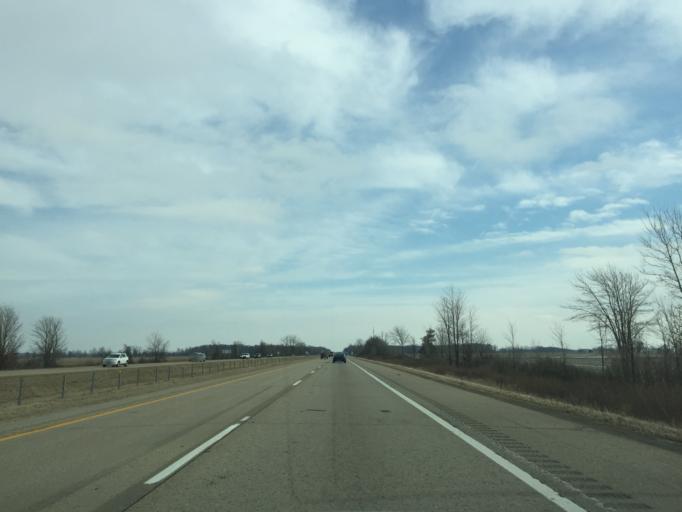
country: US
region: Michigan
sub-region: Ionia County
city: Lake Odessa
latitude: 42.8791
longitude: -85.1197
